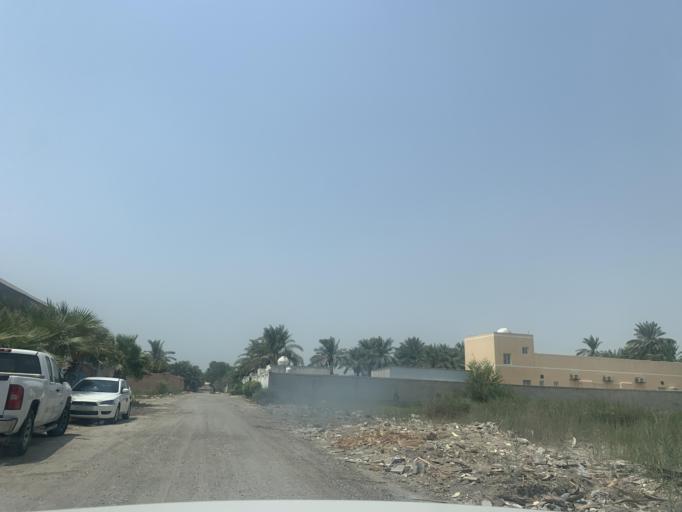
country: BH
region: Central Governorate
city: Madinat Hamad
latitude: 26.1208
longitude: 50.4685
